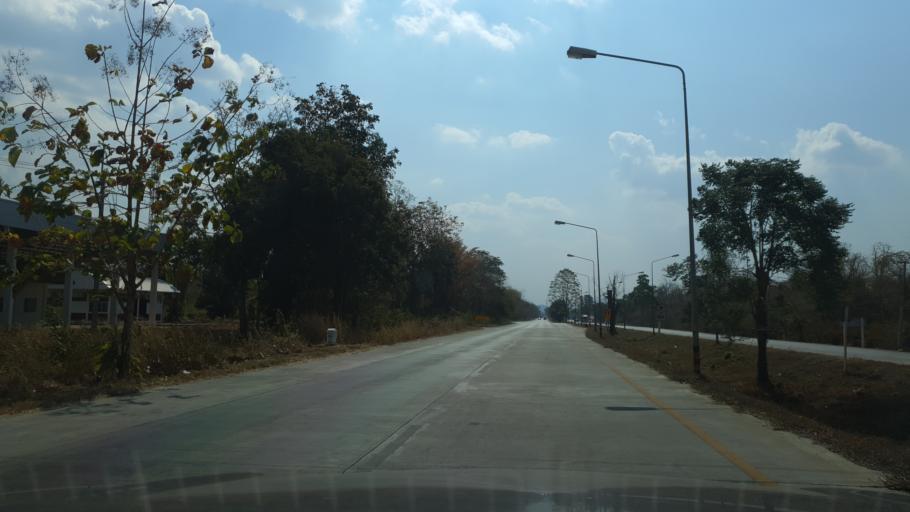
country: TH
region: Lampang
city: Mae Phrik
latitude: 17.4422
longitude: 99.1591
